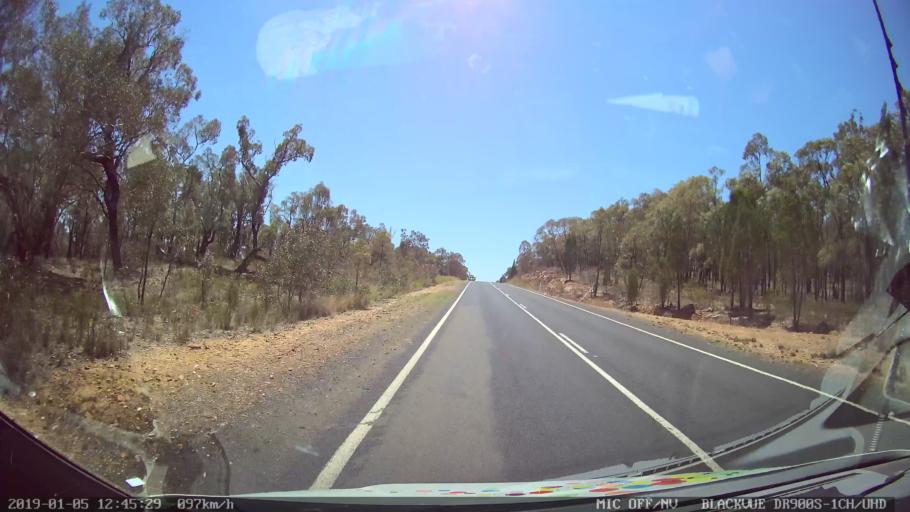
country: AU
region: New South Wales
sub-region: Warrumbungle Shire
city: Coonabarabran
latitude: -31.1272
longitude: 149.5507
